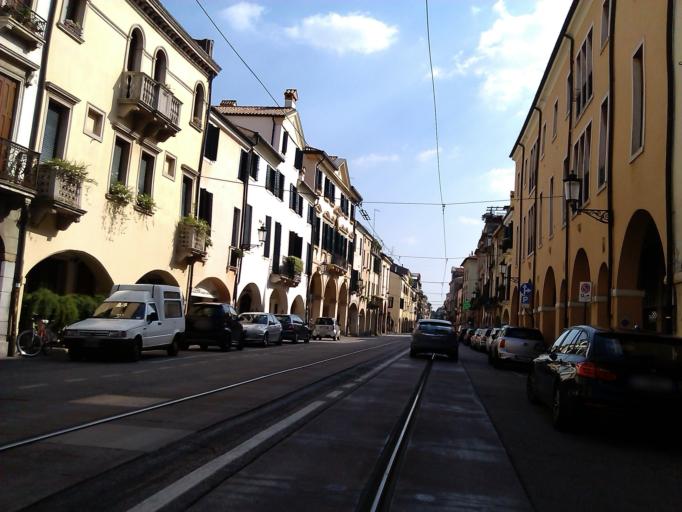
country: IT
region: Veneto
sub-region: Provincia di Padova
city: Padova
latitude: 45.3965
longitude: 11.8737
